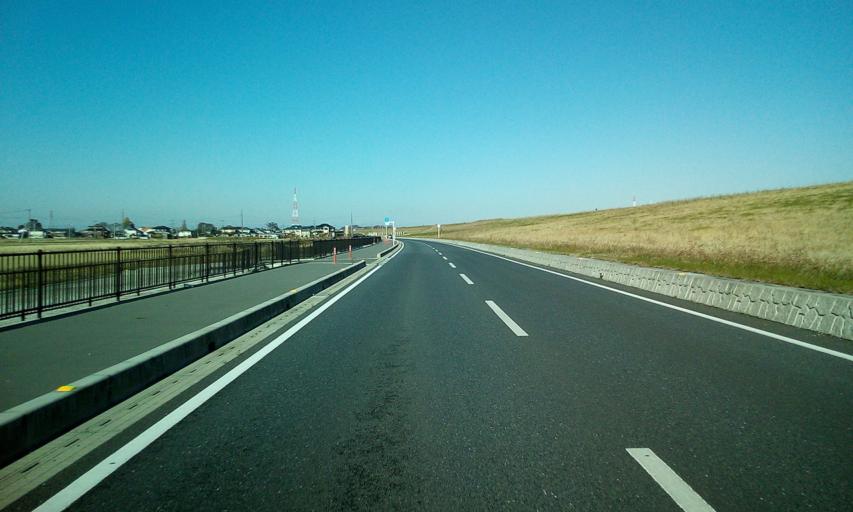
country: JP
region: Chiba
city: Noda
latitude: 35.9194
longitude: 139.8653
